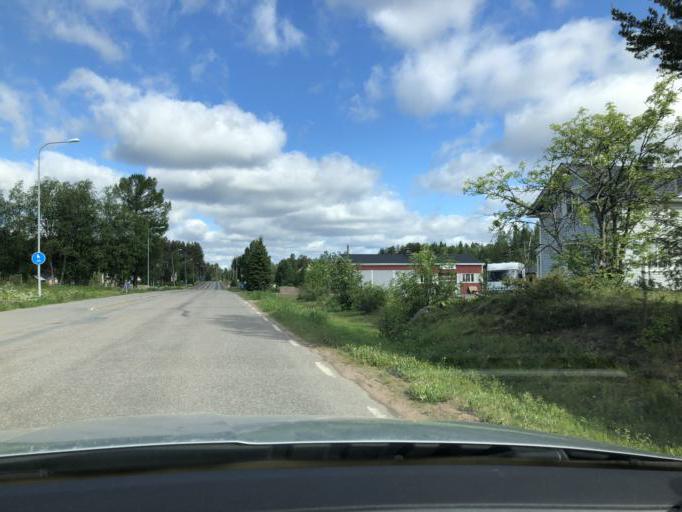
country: SE
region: Norrbotten
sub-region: Pajala Kommun
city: Pajala
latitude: 67.2206
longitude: 23.3494
